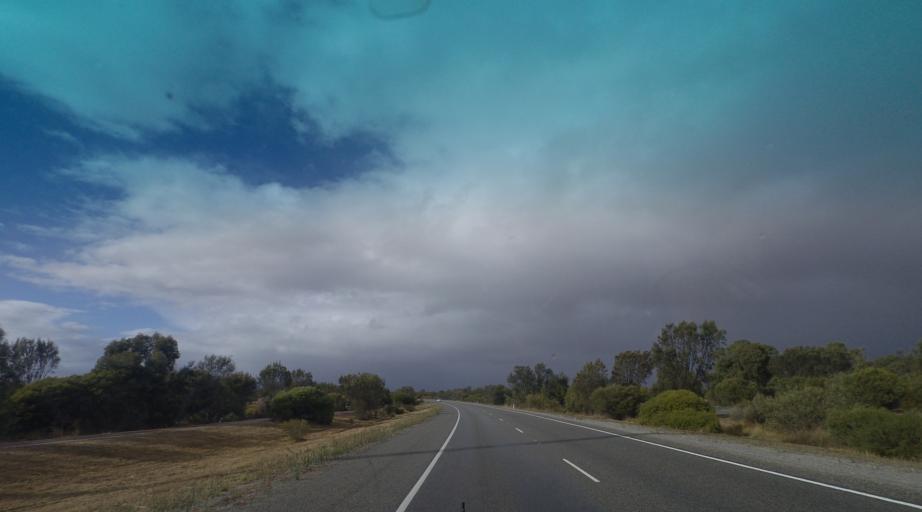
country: AU
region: Western Australia
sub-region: Serpentine-Jarrahdale
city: Oakford
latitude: -32.1972
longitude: 115.9626
